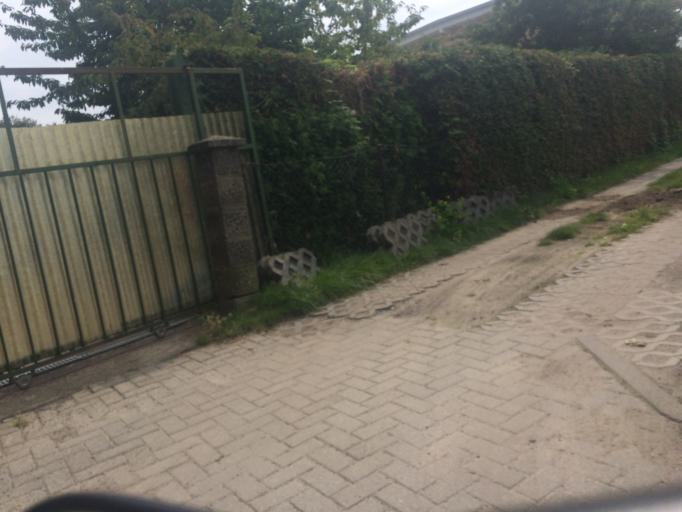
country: DE
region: Berlin
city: Heinersdorf
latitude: 52.5689
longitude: 13.4359
